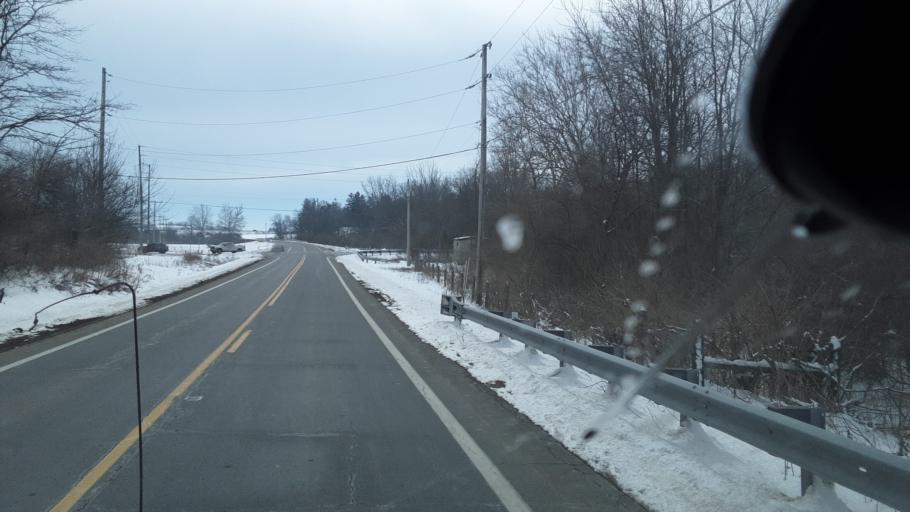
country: US
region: Ohio
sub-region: Madison County
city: Choctaw Lake
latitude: 39.9491
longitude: -83.5034
